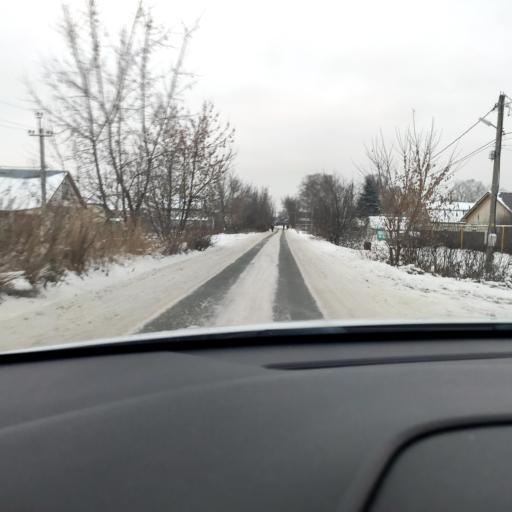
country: RU
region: Tatarstan
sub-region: Gorod Kazan'
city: Kazan
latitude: 55.8736
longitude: 49.1498
